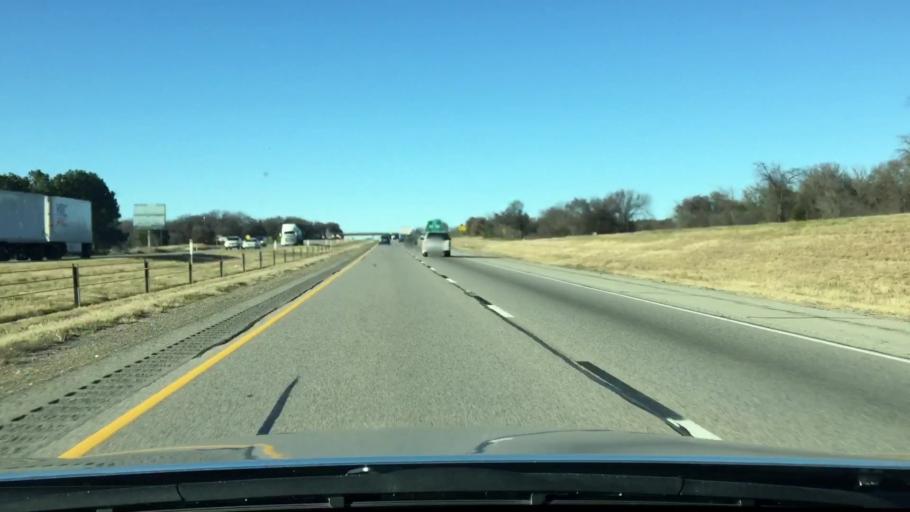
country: US
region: Texas
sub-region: Johnson County
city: Alvarado
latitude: 32.3752
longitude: -97.2038
